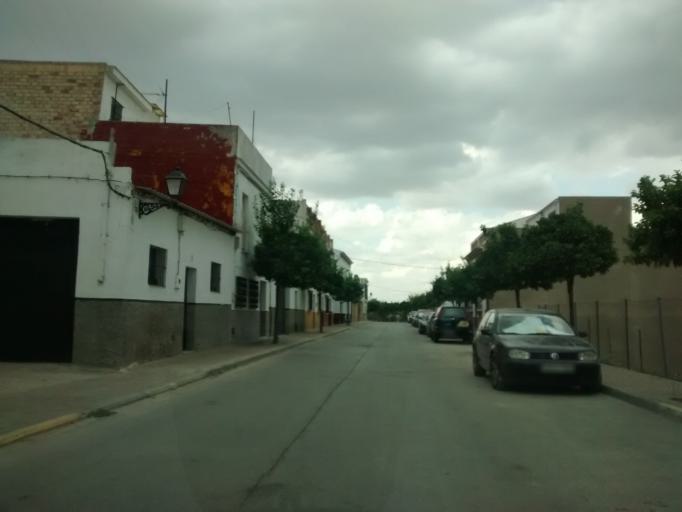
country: ES
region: Andalusia
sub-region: Provincia de Cadiz
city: Bornos
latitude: 36.8183
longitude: -5.7408
